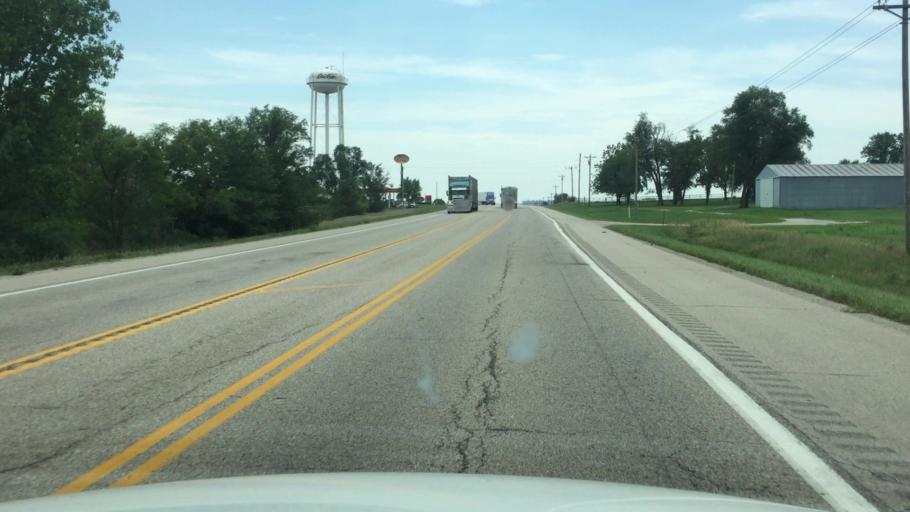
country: US
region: Kansas
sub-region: Brown County
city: Horton
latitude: 39.7057
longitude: -95.7302
